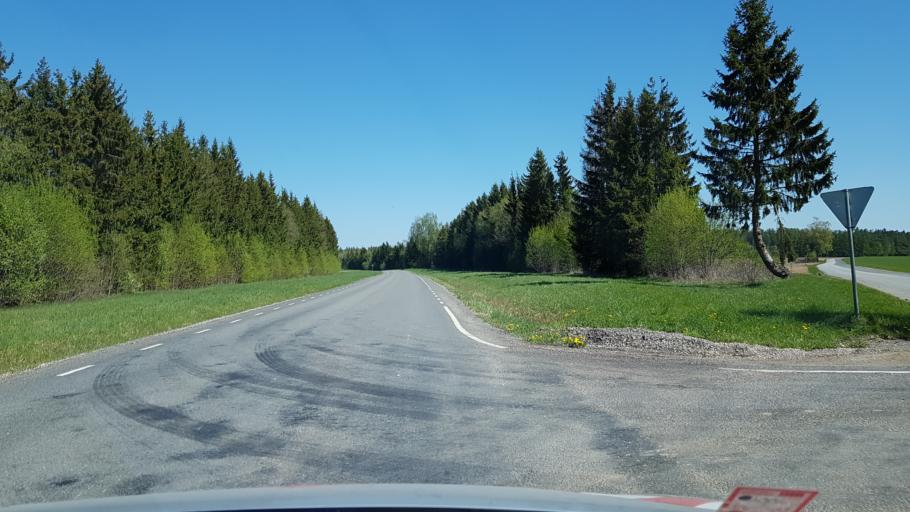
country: EE
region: Vorumaa
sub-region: Voru linn
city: Voru
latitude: 57.9521
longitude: 26.9585
